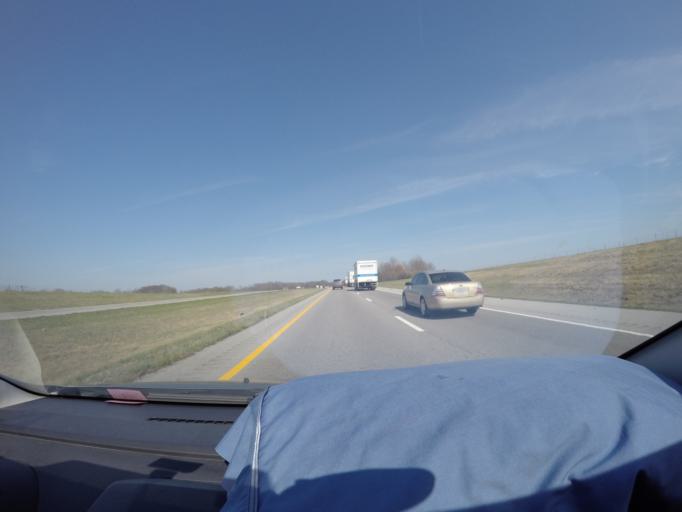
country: US
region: Tennessee
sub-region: Marion County
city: Monteagle
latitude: 35.3253
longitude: -85.9265
